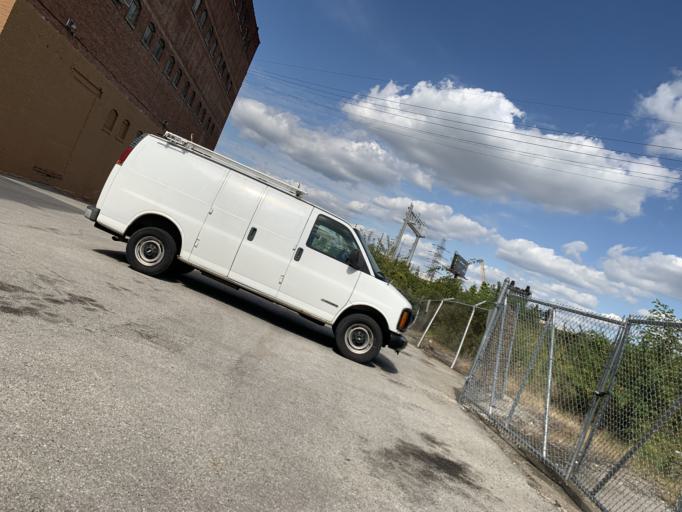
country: US
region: Kentucky
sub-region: Jefferson County
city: Louisville
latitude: 38.2612
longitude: -85.7734
